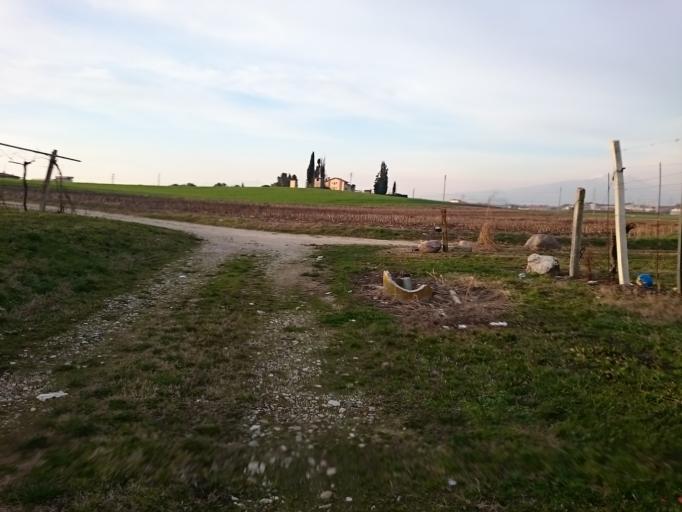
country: IT
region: Veneto
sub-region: Provincia di Verona
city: Castelnuovo del Garda
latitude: 45.4419
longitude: 10.7708
